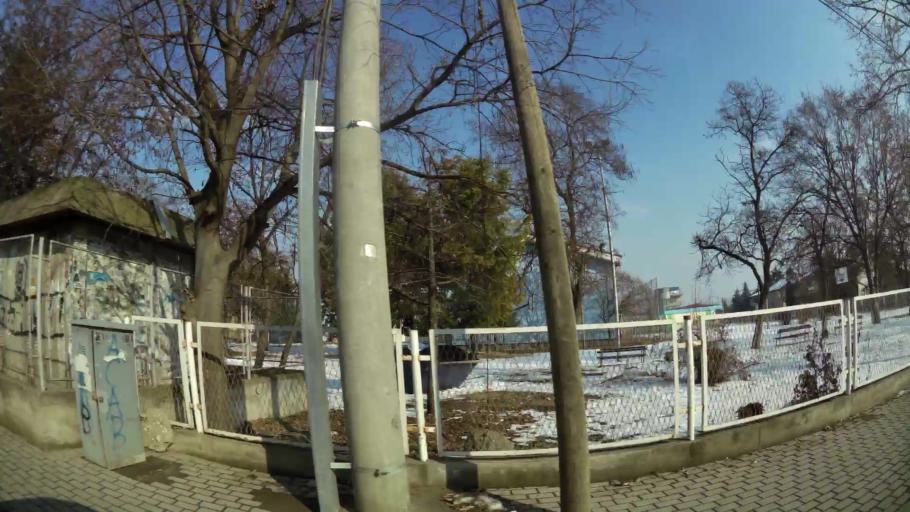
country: MK
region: Suto Orizari
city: Suto Orizare
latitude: 42.0257
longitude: 21.3827
